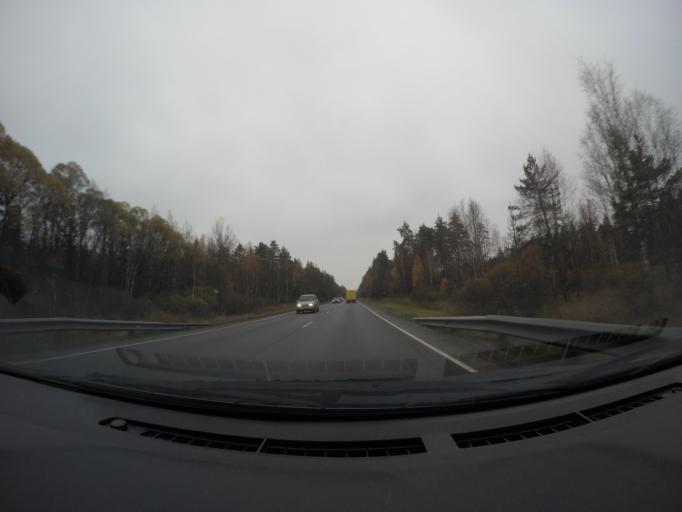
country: RU
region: Moskovskaya
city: Gzhel'
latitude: 55.5543
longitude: 38.3993
